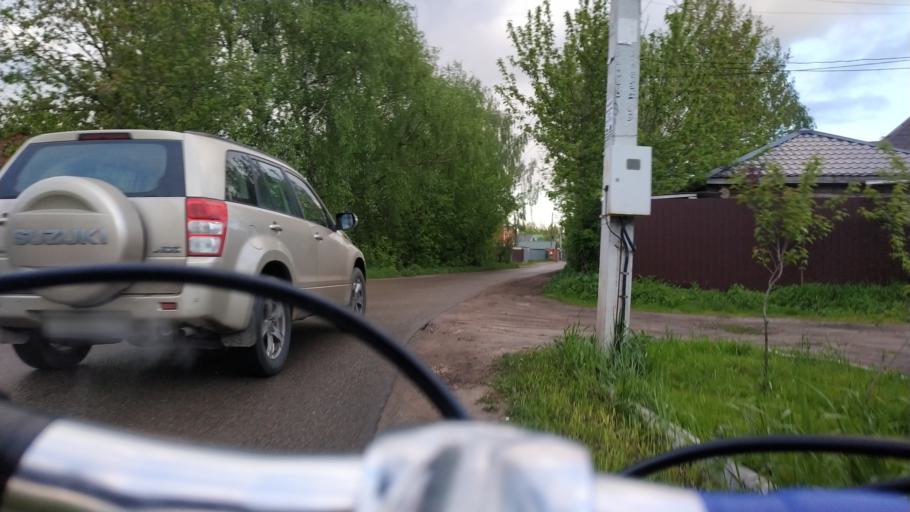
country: RU
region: Moskovskaya
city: Ramenskoye
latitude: 55.5804
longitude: 38.3006
